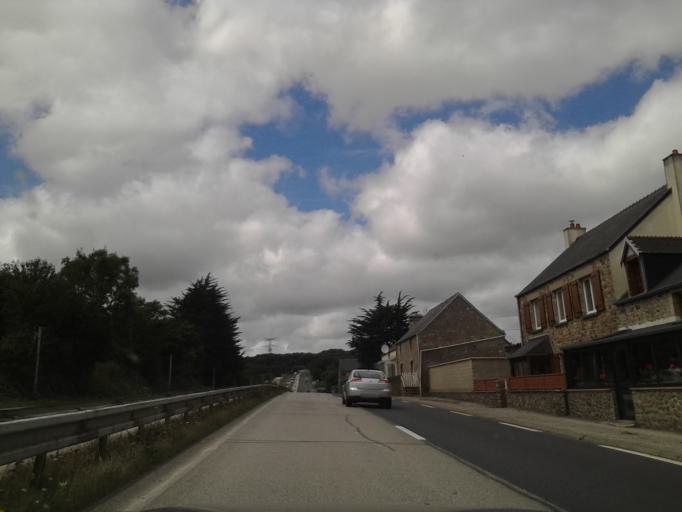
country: FR
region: Lower Normandy
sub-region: Departement de la Manche
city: Brix
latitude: 49.5425
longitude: -1.5487
